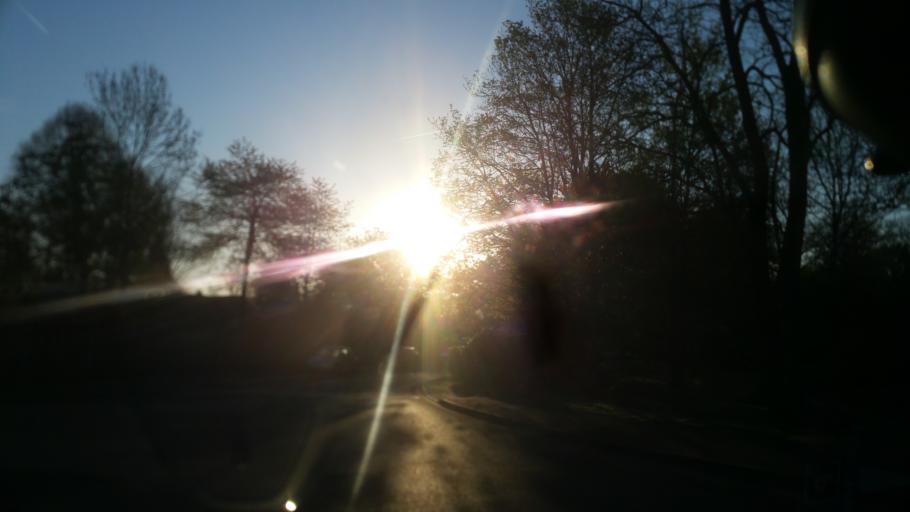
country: FR
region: Ile-de-France
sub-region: Departement de l'Essonne
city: Limours
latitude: 48.6438
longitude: 2.0757
